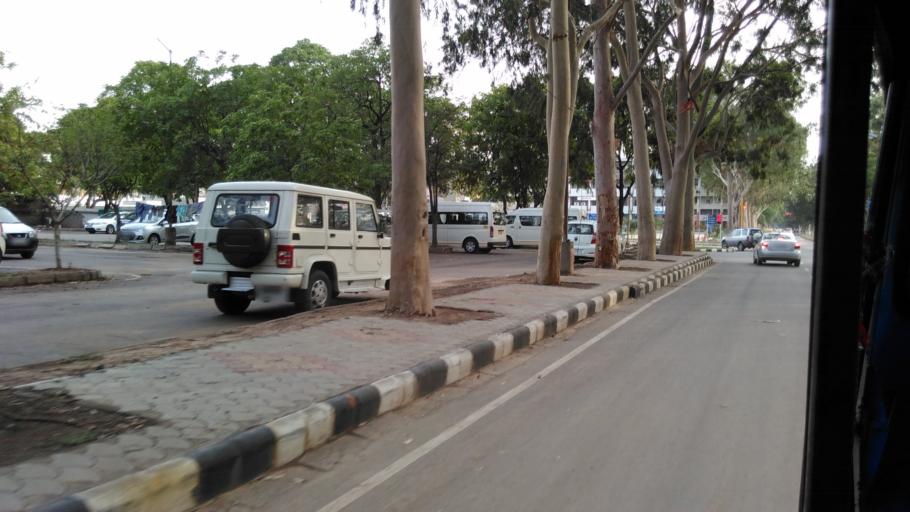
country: IN
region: Chandigarh
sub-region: Chandigarh
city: Chandigarh
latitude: 30.7429
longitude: 76.7822
